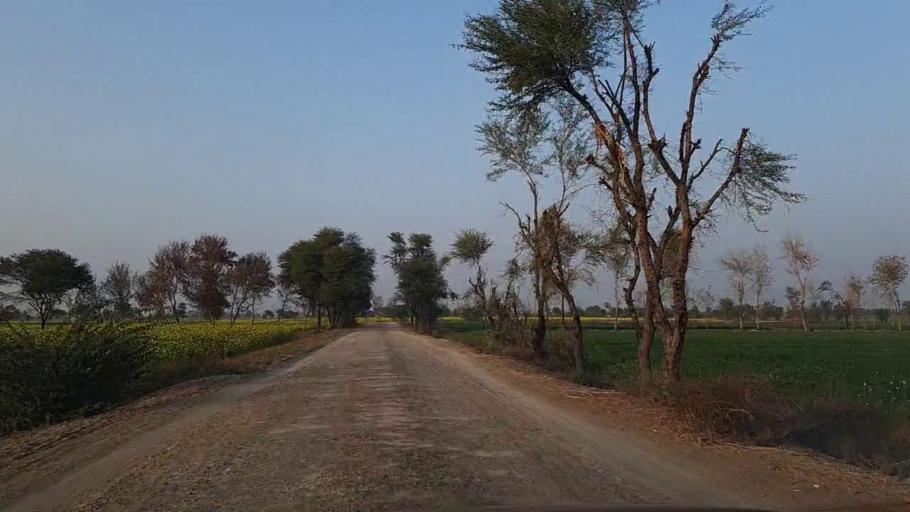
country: PK
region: Sindh
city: Daur
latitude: 26.4295
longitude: 68.3859
